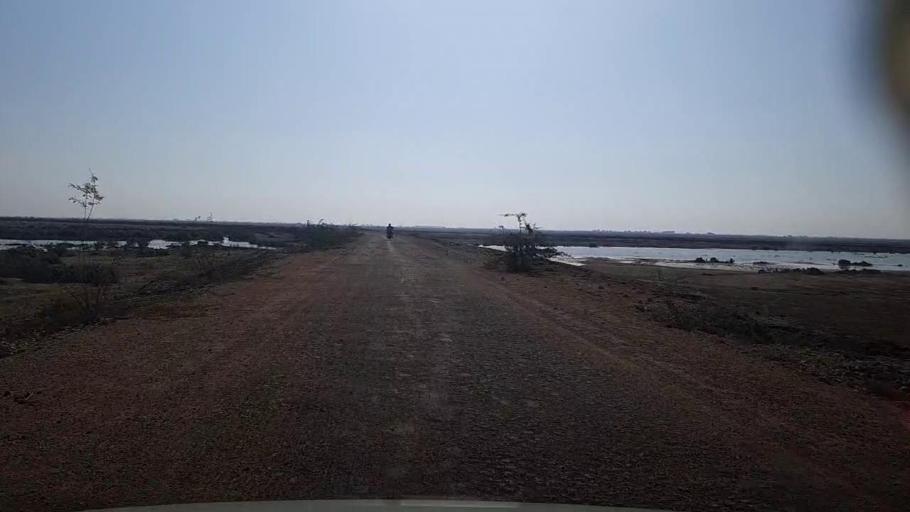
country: PK
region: Sindh
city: Mirpur Sakro
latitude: 24.5182
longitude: 67.4921
